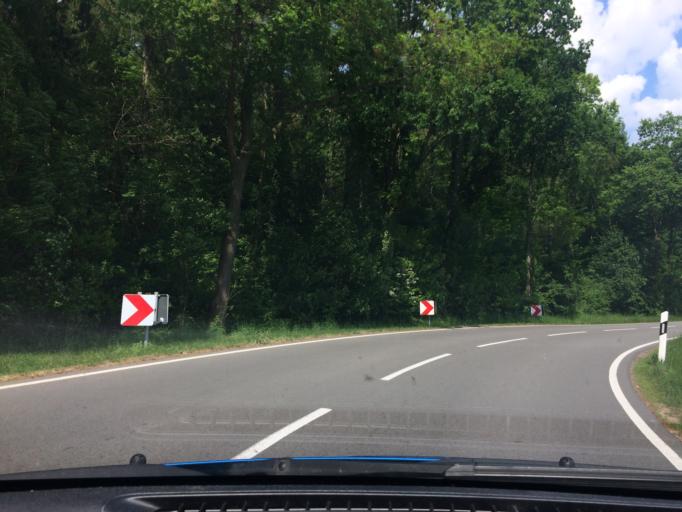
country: DE
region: Lower Saxony
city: Tosterglope
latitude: 53.1988
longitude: 10.7969
